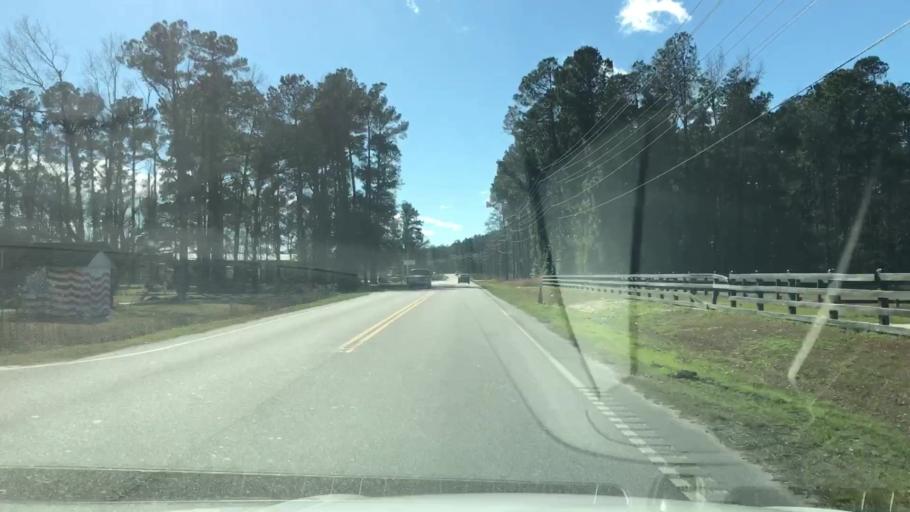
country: US
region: South Carolina
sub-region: Dorchester County
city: Summerville
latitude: 33.0777
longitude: -80.2132
